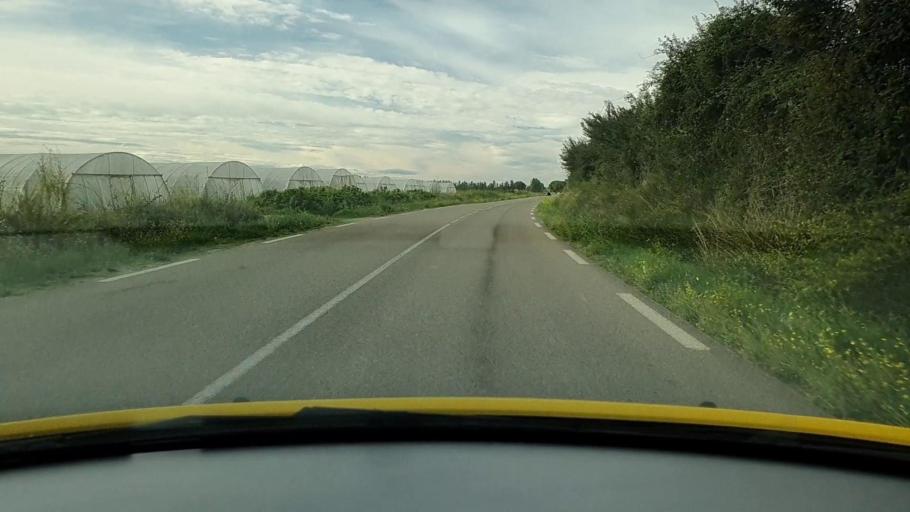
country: FR
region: Languedoc-Roussillon
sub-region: Departement du Gard
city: Bellegarde
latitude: 43.7669
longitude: 4.5312
